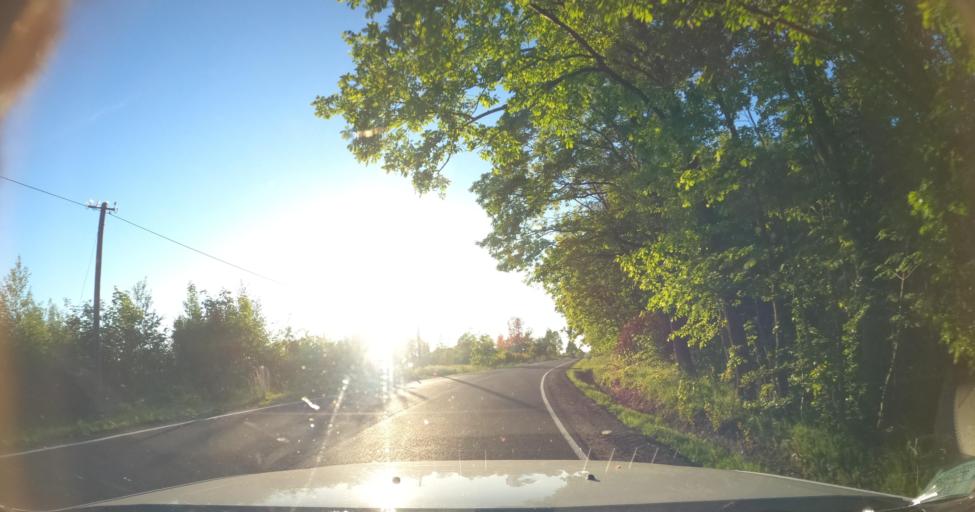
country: PL
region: Pomeranian Voivodeship
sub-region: Powiat bytowski
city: Czarna Dabrowka
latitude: 54.3462
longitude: 17.5854
